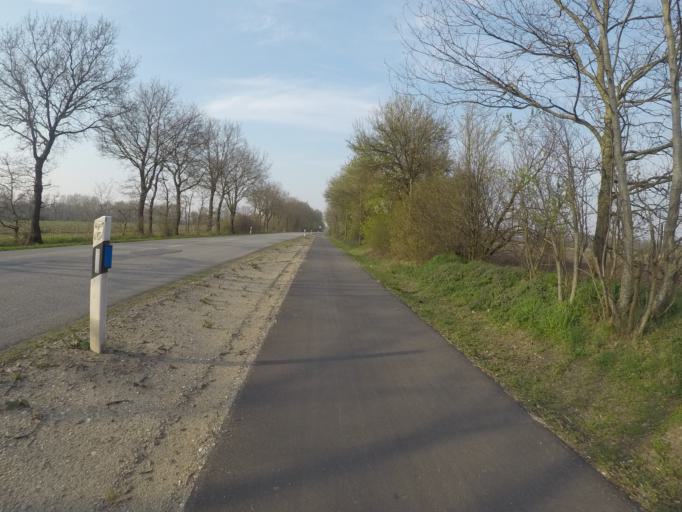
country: DE
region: Schleswig-Holstein
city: Wahlstedt
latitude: 53.9754
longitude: 10.1877
